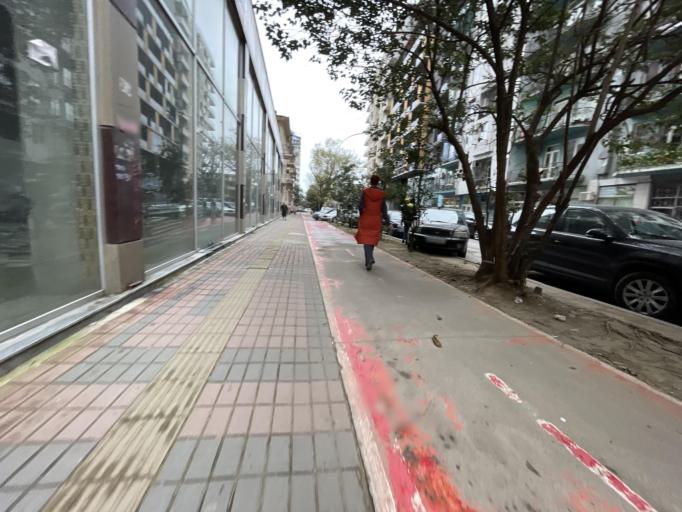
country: GE
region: Ajaria
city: Batumi
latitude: 41.6435
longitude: 41.6289
